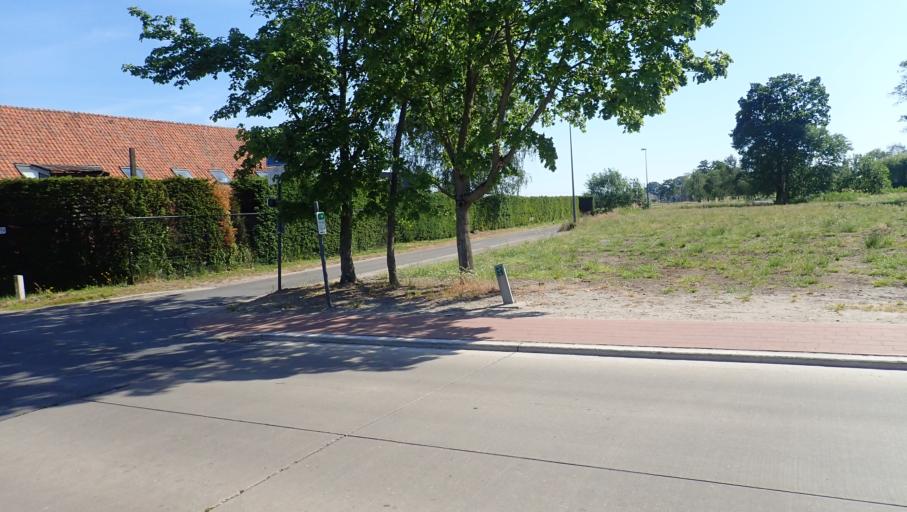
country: BE
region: Flanders
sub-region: Provincie Antwerpen
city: Wuustwezel
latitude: 51.3647
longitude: 4.5447
